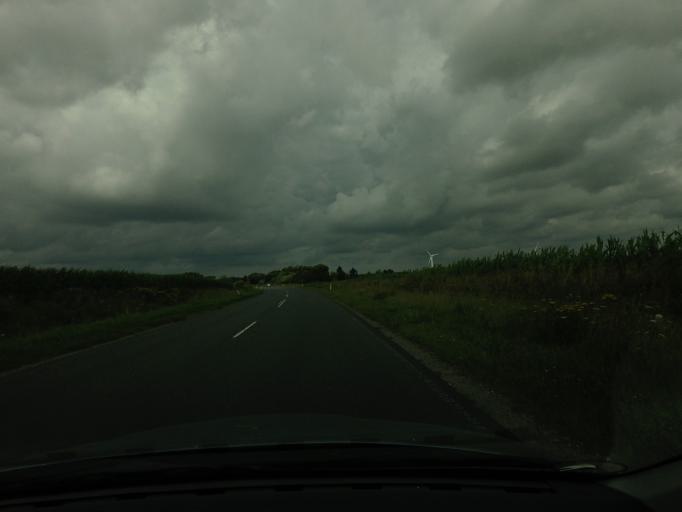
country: DK
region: North Denmark
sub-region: Hjorring Kommune
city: Tars
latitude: 57.4208
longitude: 10.0546
